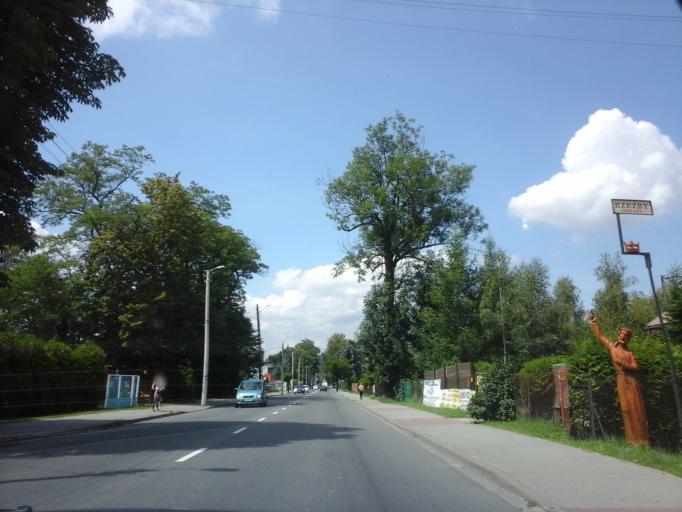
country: PL
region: Lesser Poland Voivodeship
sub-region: Powiat suski
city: Makow Podhalanski
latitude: 49.7271
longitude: 19.6860
